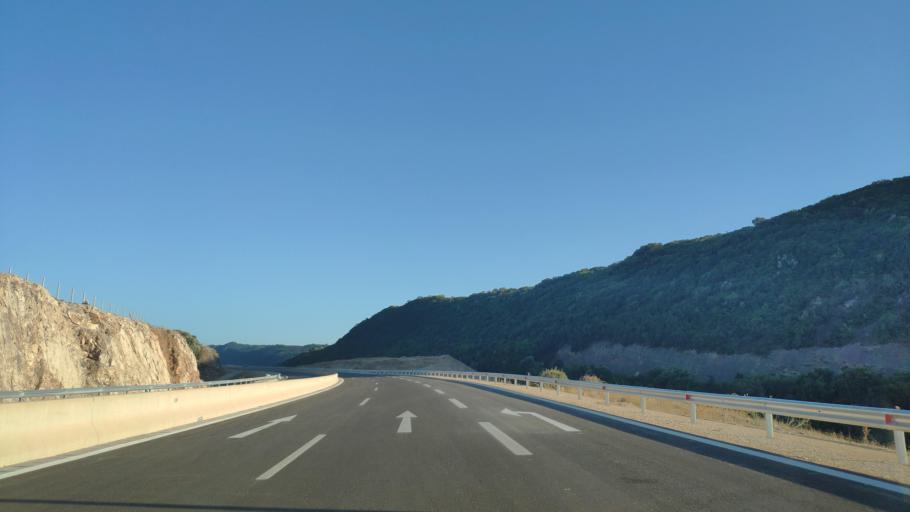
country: GR
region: West Greece
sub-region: Nomos Aitolias kai Akarnanias
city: Katouna
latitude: 38.7860
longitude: 21.1427
